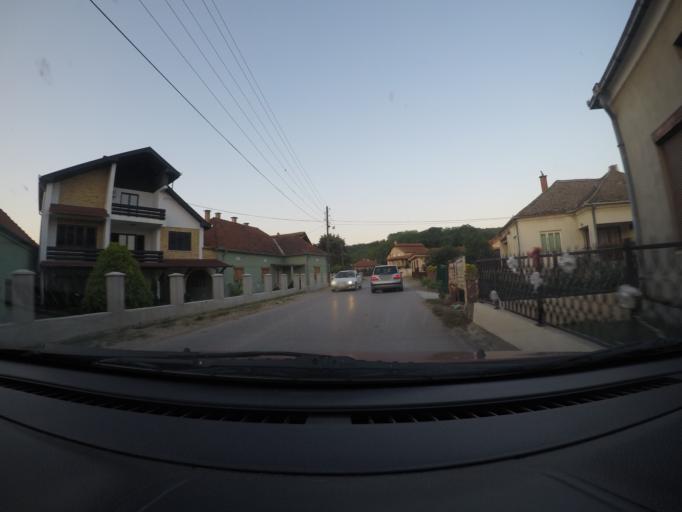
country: RS
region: Central Serbia
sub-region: Branicevski Okrug
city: Veliko Gradiste
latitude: 44.6677
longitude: 21.5187
